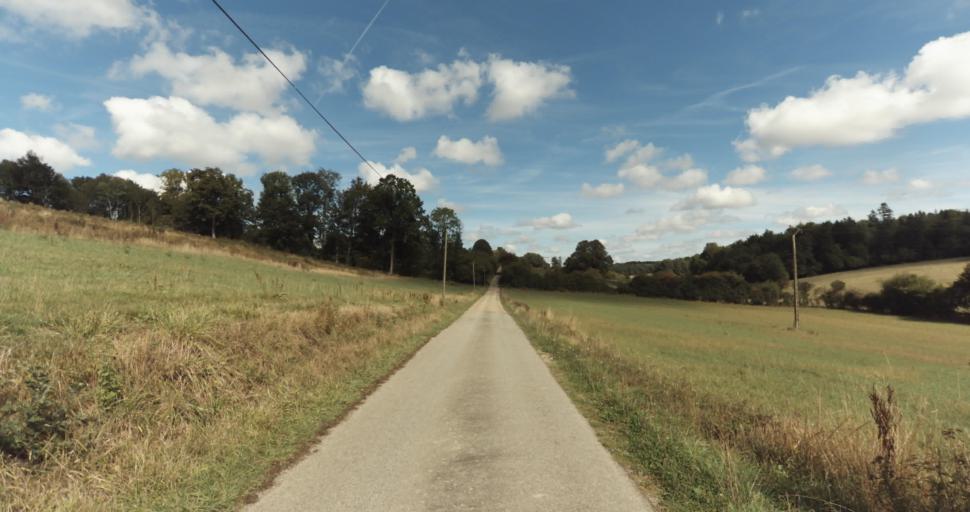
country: FR
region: Lower Normandy
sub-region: Departement du Calvados
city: Orbec
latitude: 48.9024
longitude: 0.3743
